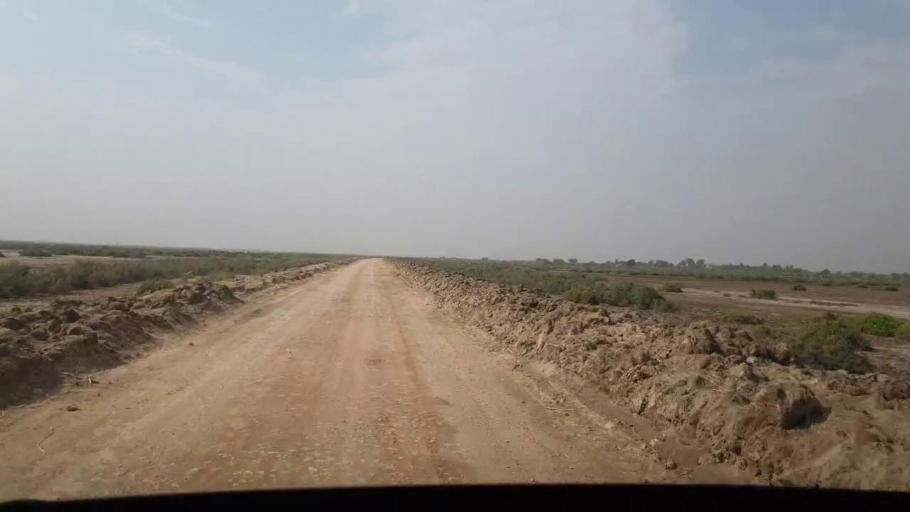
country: PK
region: Sindh
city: Chuhar Jamali
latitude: 24.3577
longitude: 67.9290
